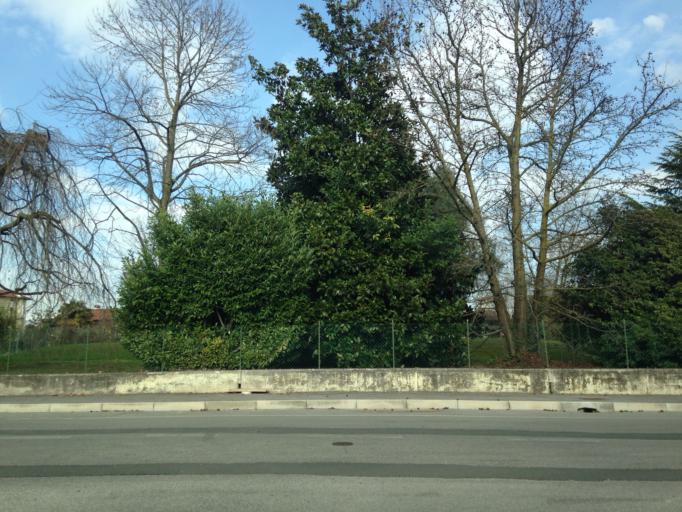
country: IT
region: Friuli Venezia Giulia
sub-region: Provincia di Pordenone
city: Sacile
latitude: 45.9459
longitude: 12.5095
